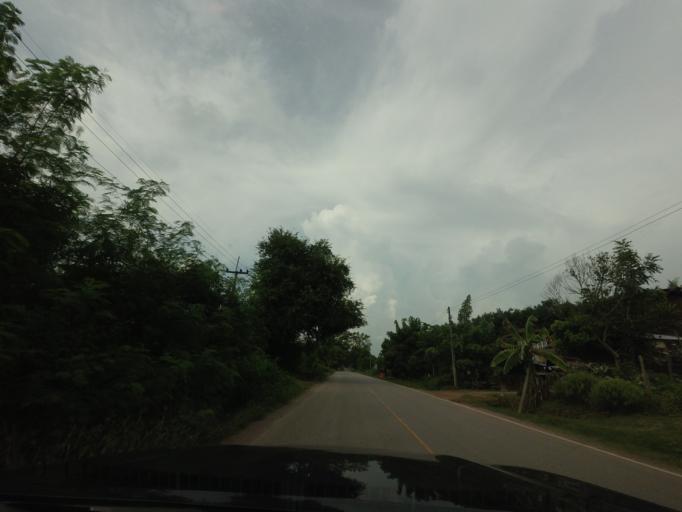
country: TH
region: Changwat Nong Bua Lamphu
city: Suwannakhuha
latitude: 17.4489
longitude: 102.3453
